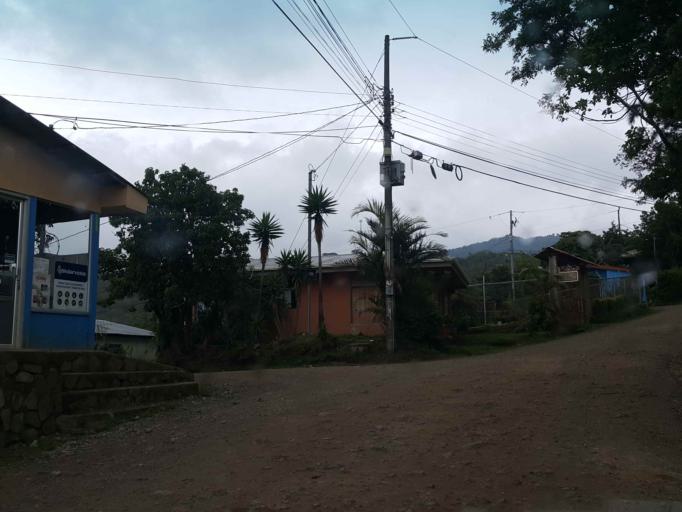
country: CR
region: Guanacaste
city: Juntas
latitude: 10.3146
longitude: -84.8342
